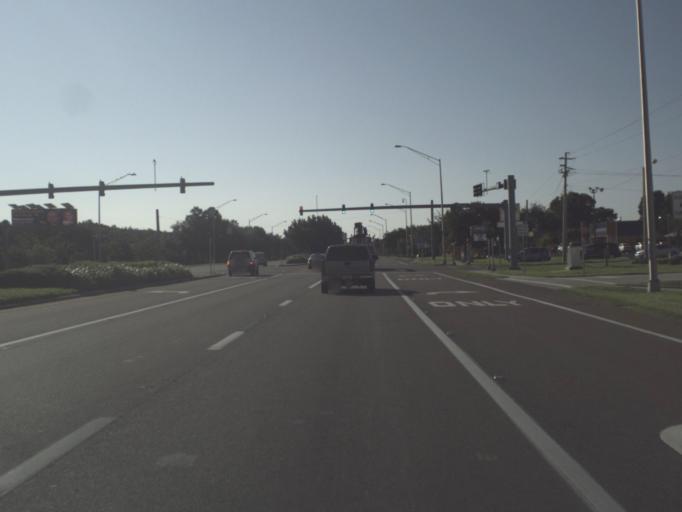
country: US
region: Florida
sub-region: Lee County
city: North Fort Myers
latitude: 26.6604
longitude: -81.8842
